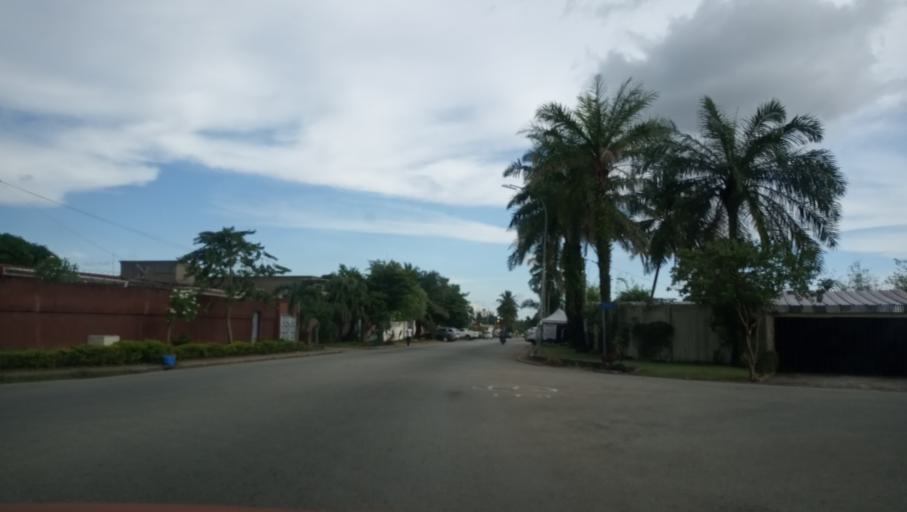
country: CI
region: Lagunes
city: Abidjan
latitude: 5.3480
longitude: -3.9801
